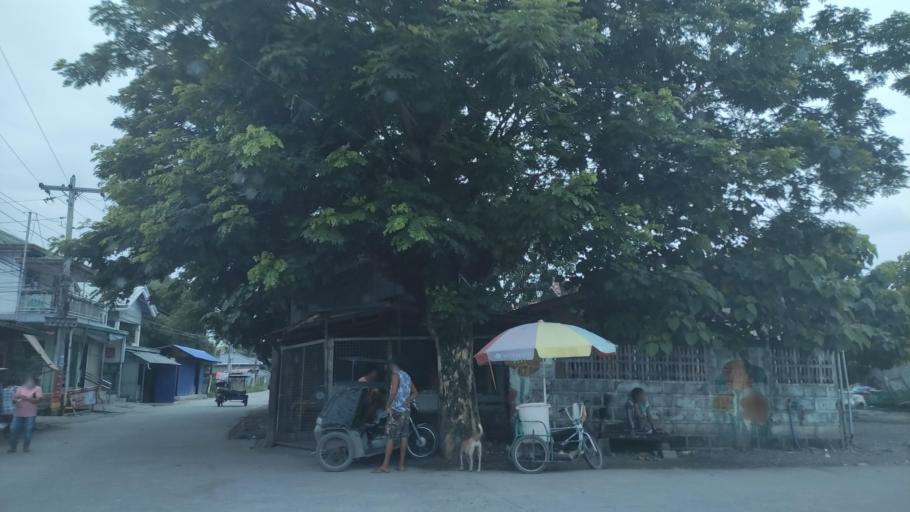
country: PH
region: Central Luzon
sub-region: Province of Nueva Ecija
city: San Anton
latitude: 15.3592
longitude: 120.9046
